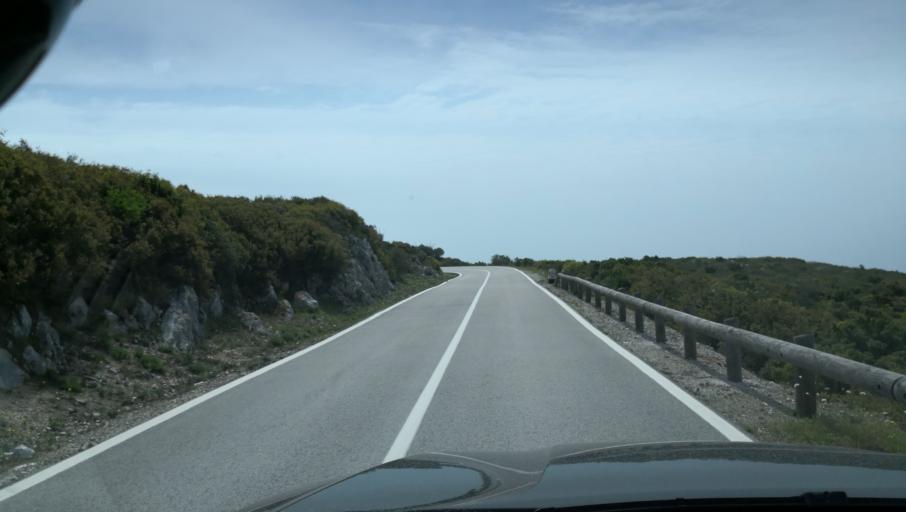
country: PT
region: Setubal
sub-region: Palmela
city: Quinta do Anjo
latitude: 38.4931
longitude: -8.9628
